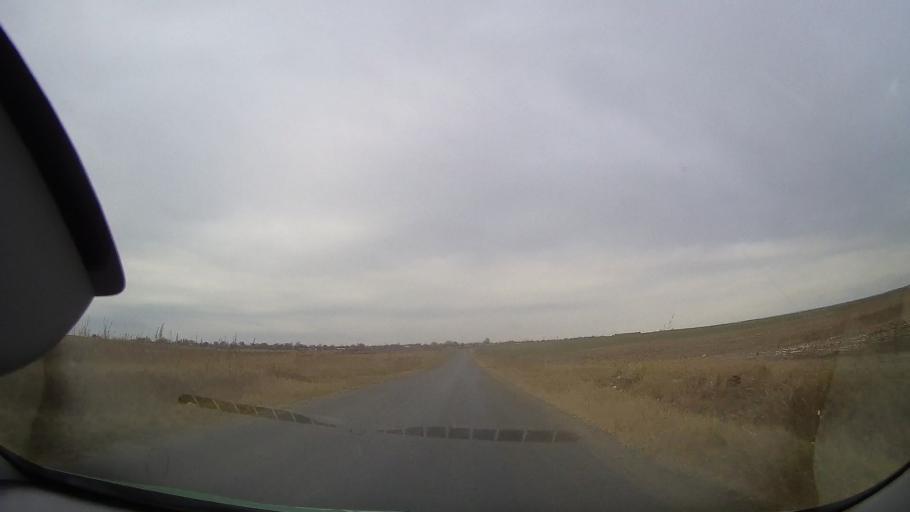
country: RO
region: Buzau
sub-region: Comuna Largu
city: Largu
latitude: 44.9737
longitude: 27.1607
